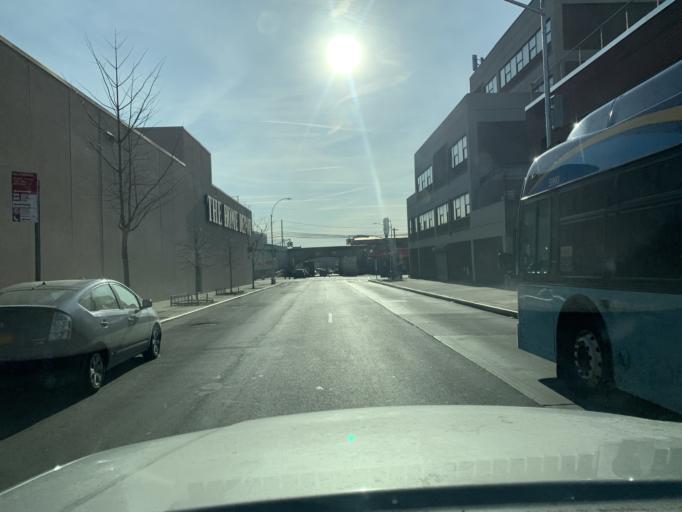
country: US
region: New York
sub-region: Queens County
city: Jamaica
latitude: 40.7050
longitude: -73.7933
